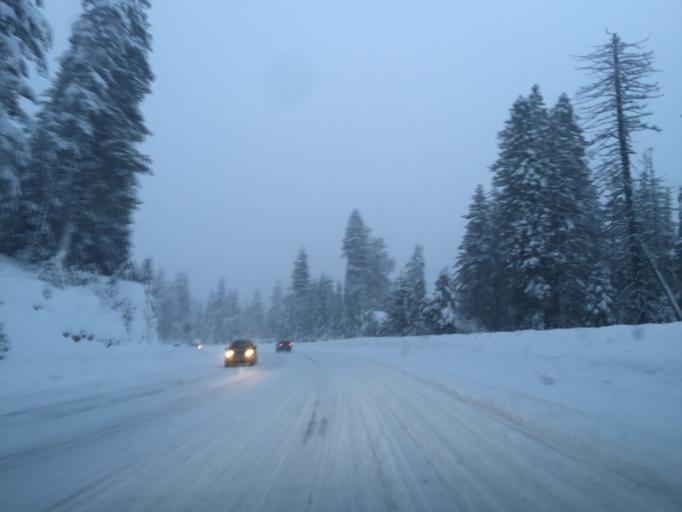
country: US
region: Washington
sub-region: Chelan County
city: Leavenworth
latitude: 47.7827
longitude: -120.8974
